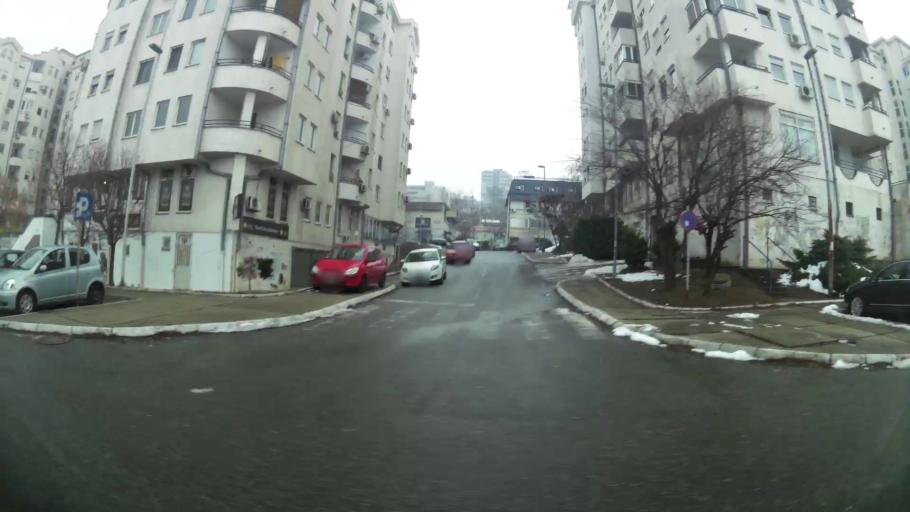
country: RS
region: Central Serbia
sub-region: Belgrade
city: Vozdovac
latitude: 44.7658
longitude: 20.4965
